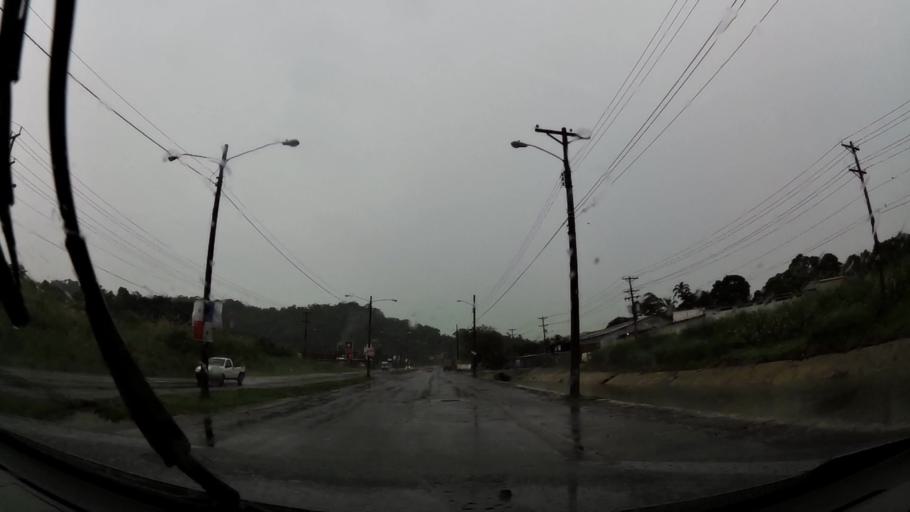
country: PA
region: Colon
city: Sabanitas
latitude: 9.3508
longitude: -79.8130
